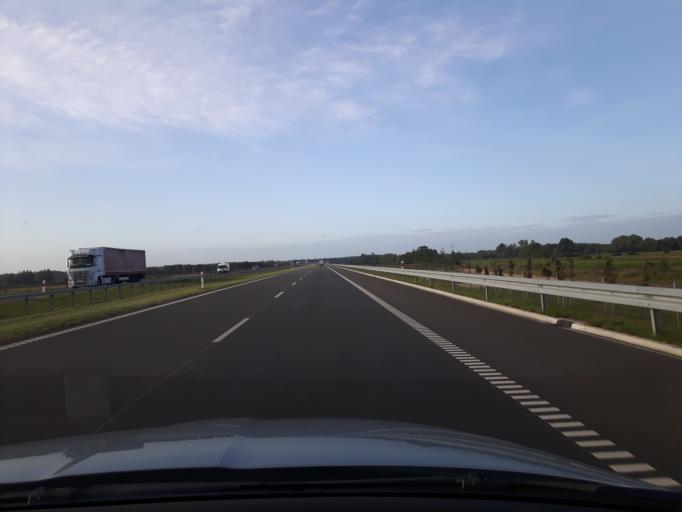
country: PL
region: Masovian Voivodeship
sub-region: Powiat radomski
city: Jedlinsk
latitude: 51.5038
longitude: 21.0801
